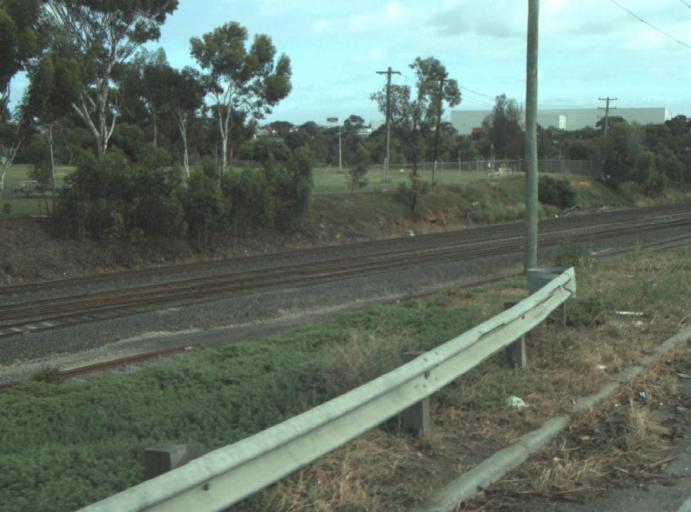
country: AU
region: Victoria
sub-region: Greater Geelong
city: Bell Park
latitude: -38.1082
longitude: 144.3569
